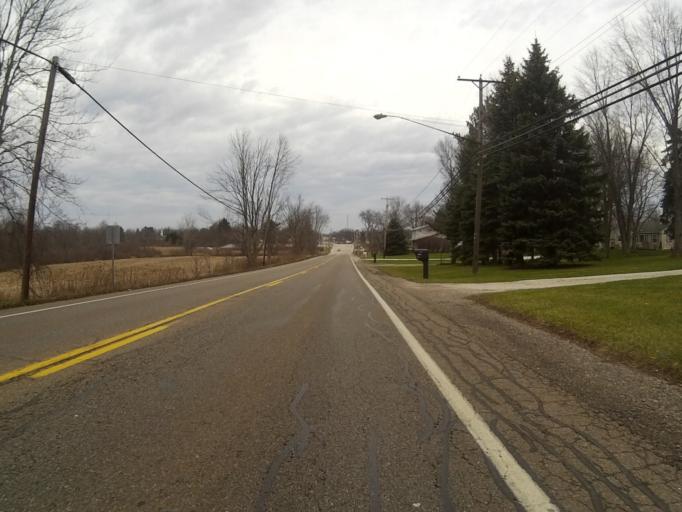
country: US
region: Ohio
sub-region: Portage County
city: Brimfield
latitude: 41.0946
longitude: -81.3463
